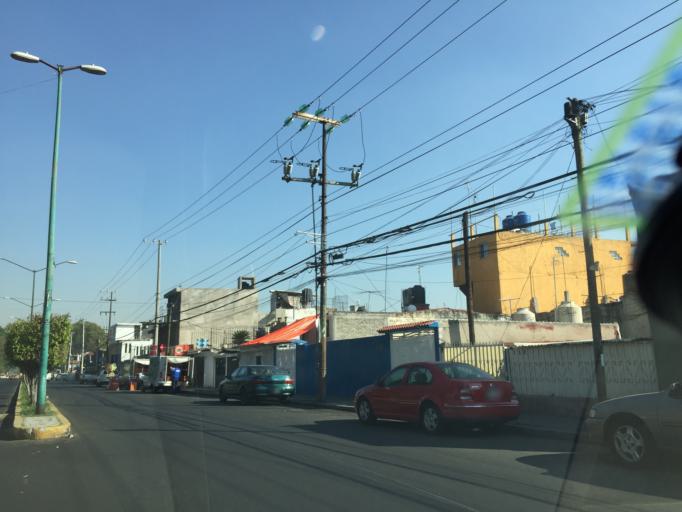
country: MX
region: Mexico
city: Vista Hermosa
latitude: 19.4966
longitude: -99.2066
